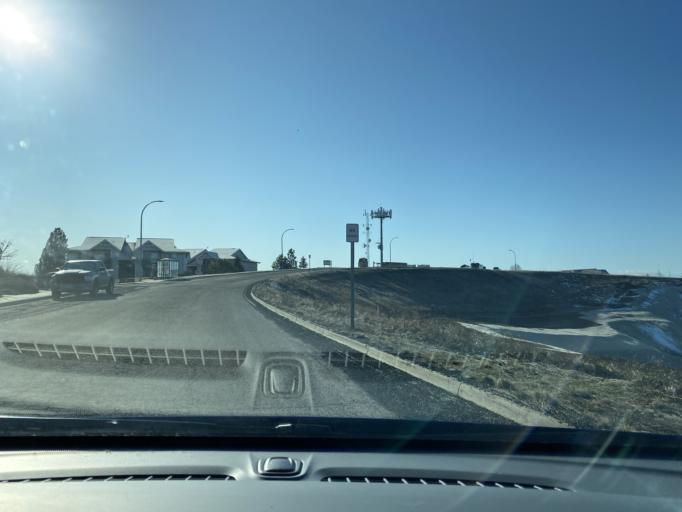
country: US
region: Washington
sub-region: Whitman County
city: Pullman
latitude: 46.7483
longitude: -117.1512
